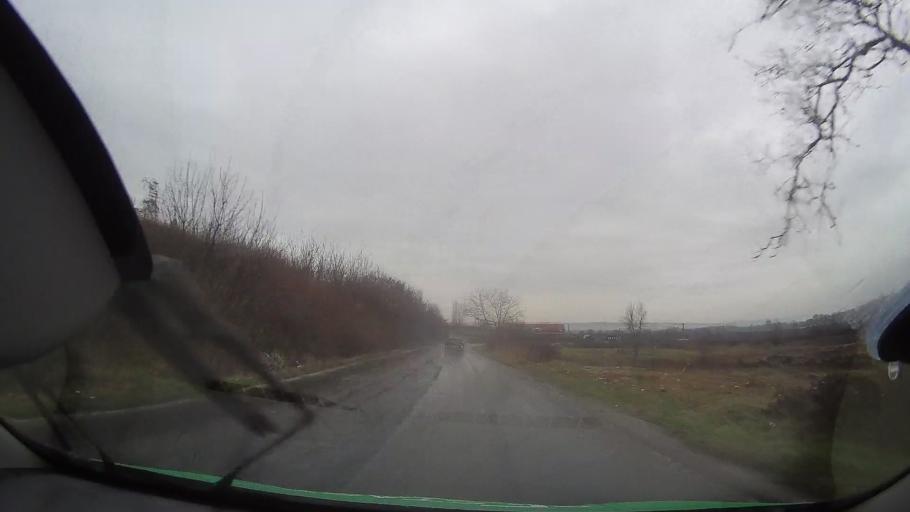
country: RO
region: Bihor
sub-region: Comuna Holod
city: Vintere
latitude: 46.7652
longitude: 22.1861
